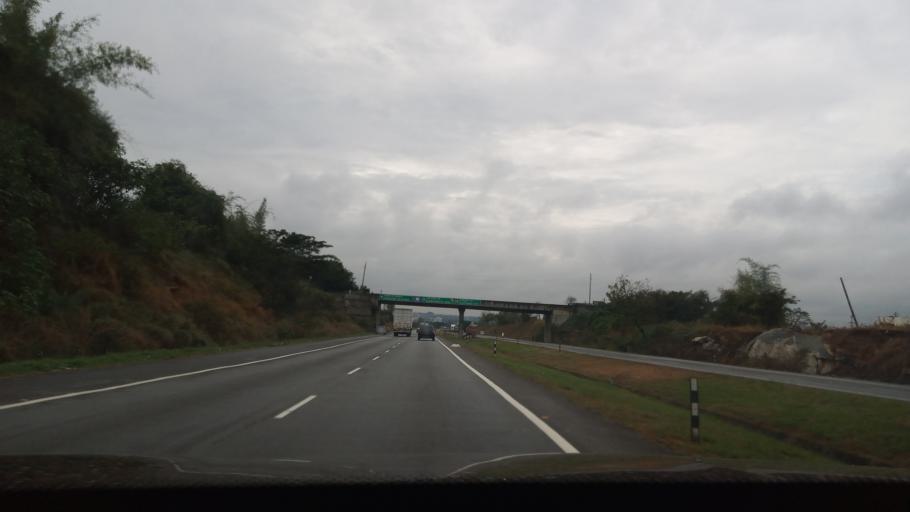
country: IN
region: Karnataka
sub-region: Bangalore Urban
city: Bangalore
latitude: 12.9636
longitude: 77.4715
